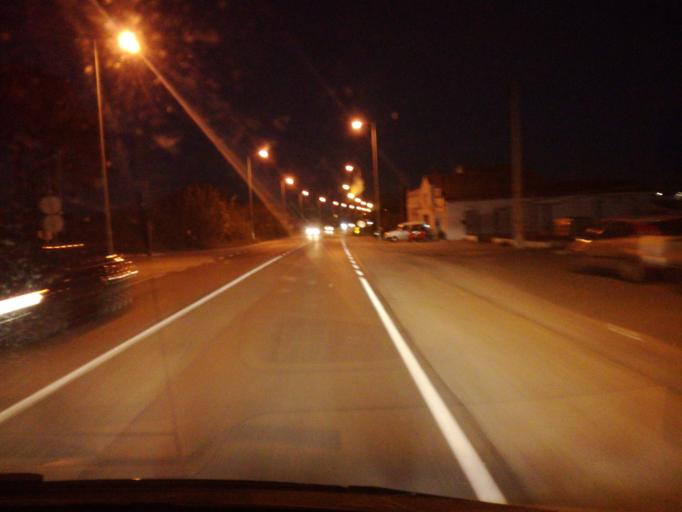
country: PT
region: Faro
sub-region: Olhao
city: Olhao
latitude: 37.0386
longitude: -7.8280
